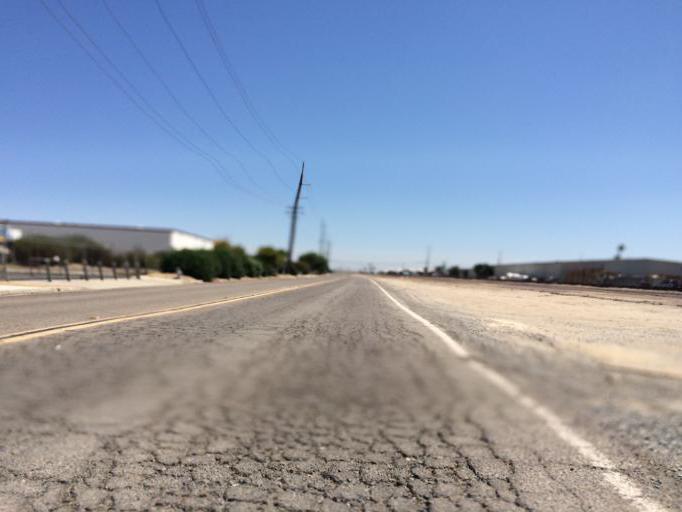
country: US
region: California
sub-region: Fresno County
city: Fresno
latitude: 36.6999
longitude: -119.7494
